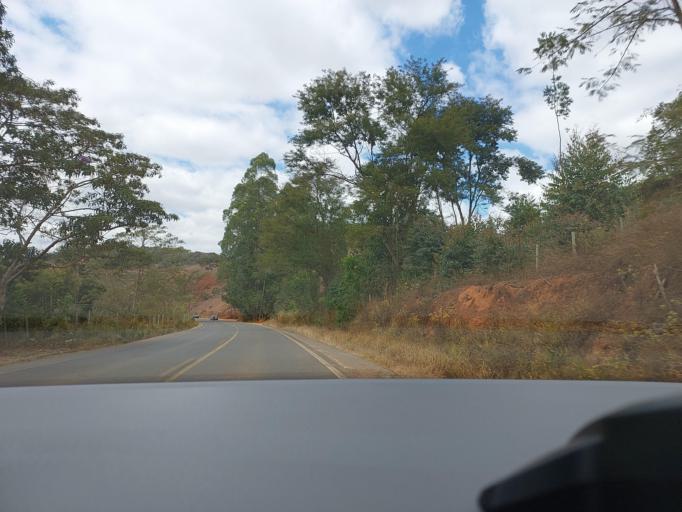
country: BR
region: Minas Gerais
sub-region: Vicosa
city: Vicosa
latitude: -20.8420
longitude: -42.6874
